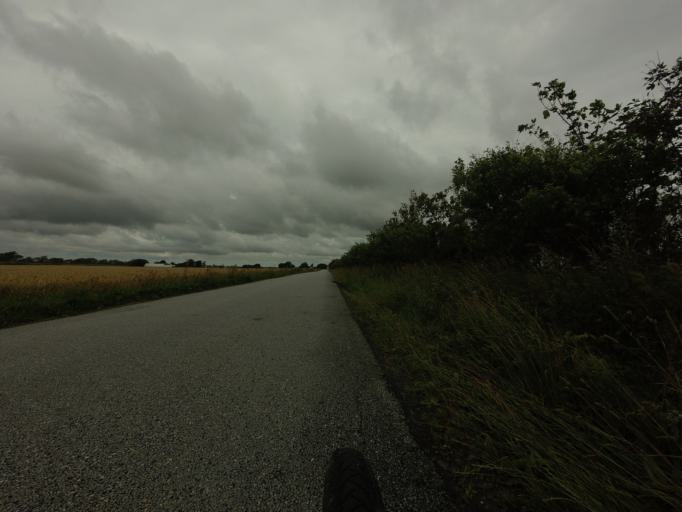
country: DK
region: North Denmark
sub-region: Bronderslev Kommune
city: Bronderslev
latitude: 57.3029
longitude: 9.8051
